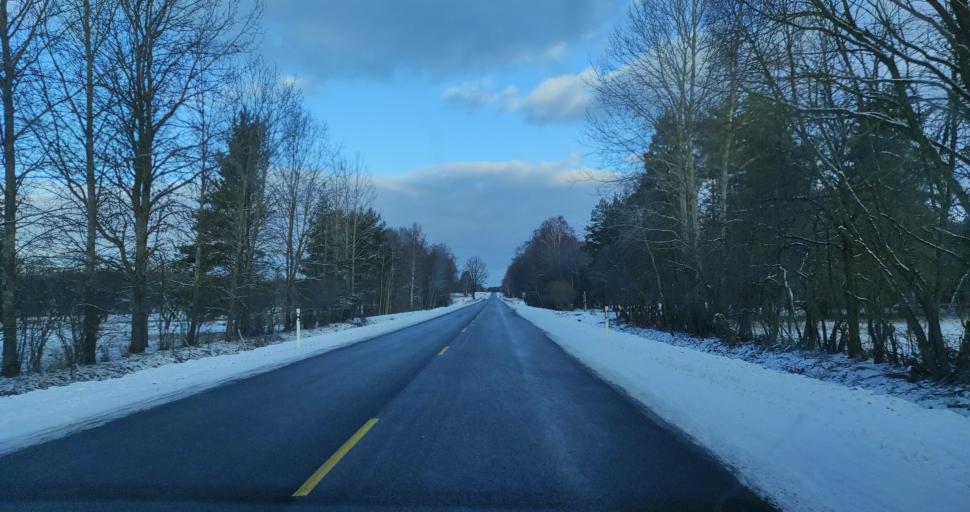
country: LV
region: Skrunda
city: Skrunda
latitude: 56.7113
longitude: 22.0126
